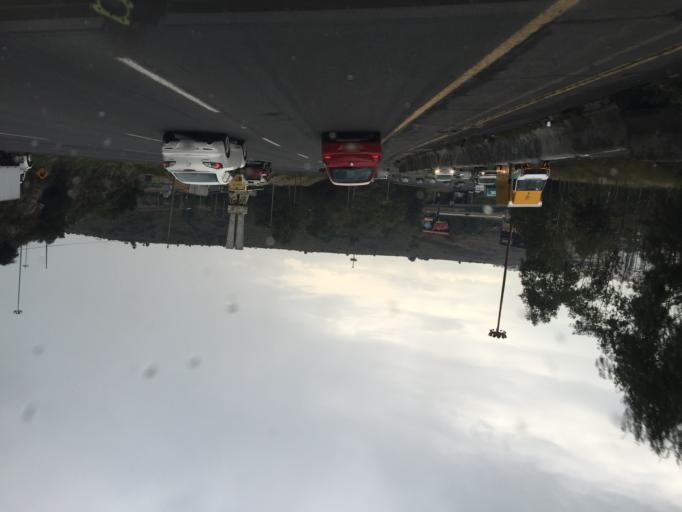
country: MX
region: Mexico
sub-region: Tultitlan
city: Buenavista
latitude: 19.5986
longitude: -99.1973
